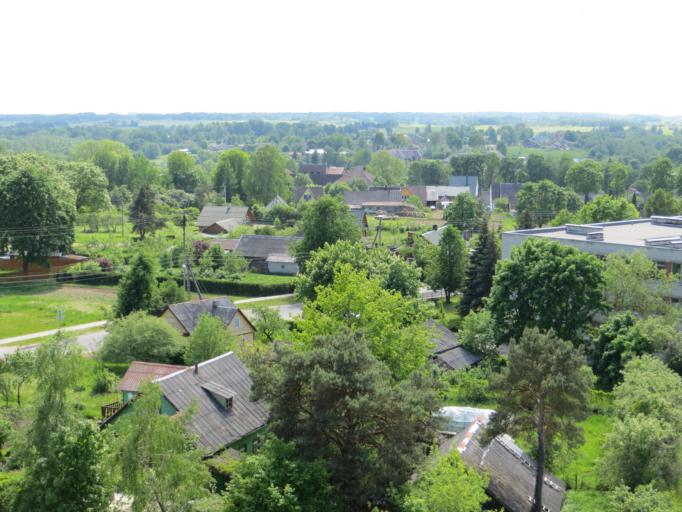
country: LT
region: Utenos apskritis
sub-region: Utena
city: Utena
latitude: 55.5891
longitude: 25.5003
